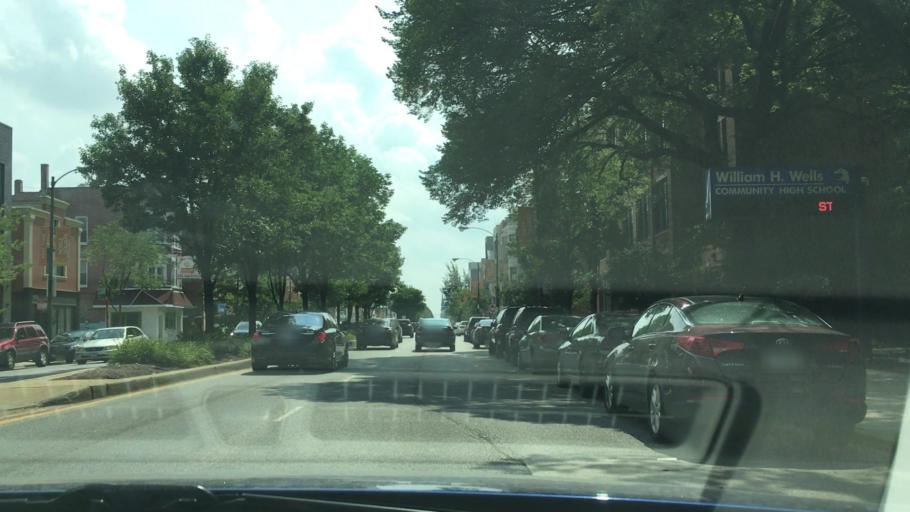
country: US
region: Illinois
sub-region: Cook County
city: Chicago
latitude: 41.8994
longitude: -87.6675
